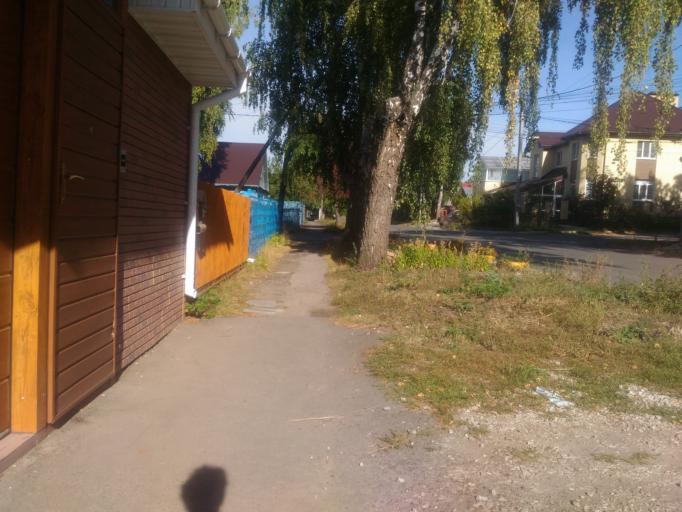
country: RU
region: Ulyanovsk
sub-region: Ulyanovskiy Rayon
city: Ulyanovsk
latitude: 54.3476
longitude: 48.3750
